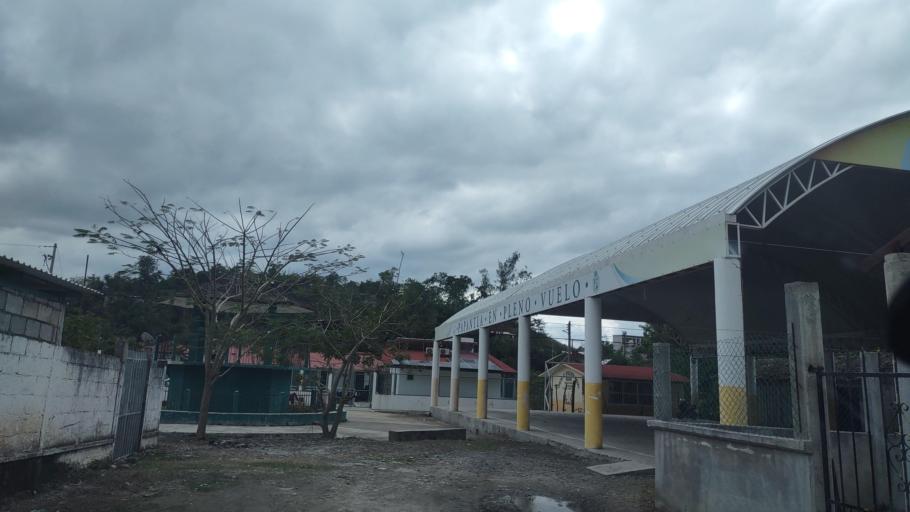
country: MX
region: Veracruz
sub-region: Papantla
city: Polutla
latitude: 20.4681
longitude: -97.2564
